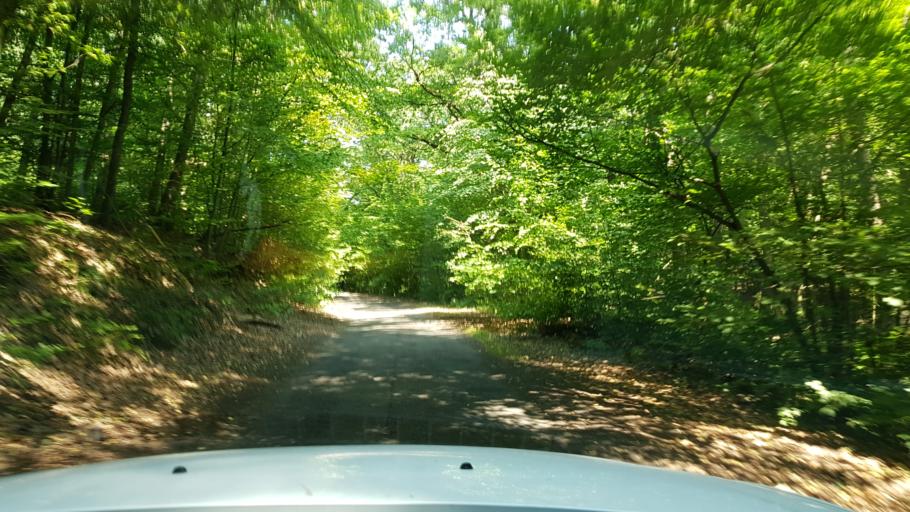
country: DE
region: Brandenburg
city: Neulewin
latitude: 52.8027
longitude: 14.3128
